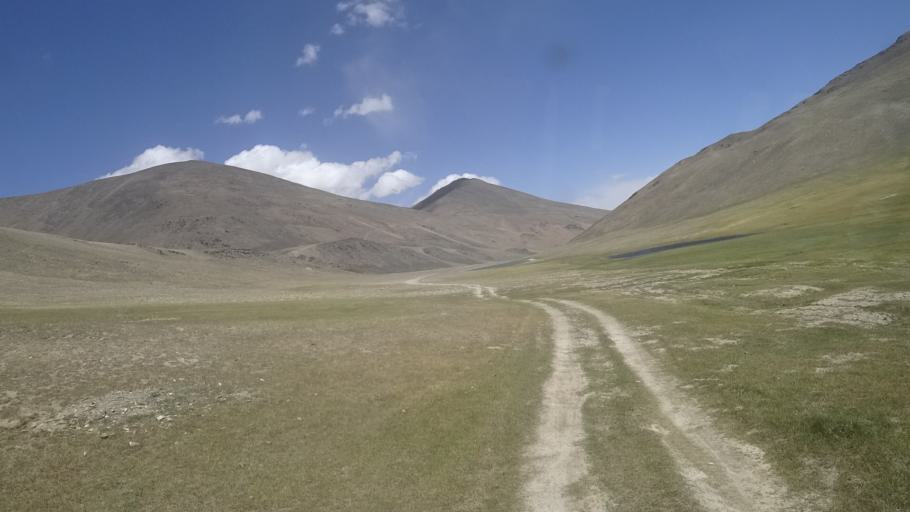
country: TJ
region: Gorno-Badakhshan
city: Murghob
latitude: 37.5171
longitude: 74.0576
